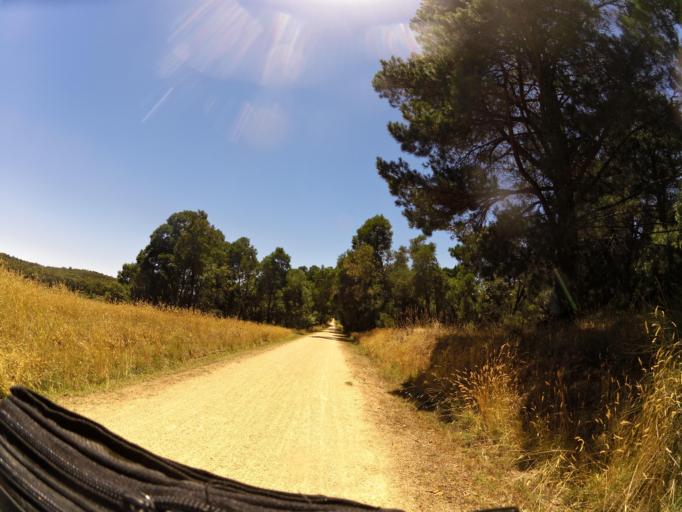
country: AU
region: Victoria
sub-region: Ballarat North
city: Delacombe
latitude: -37.6354
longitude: 143.6923
